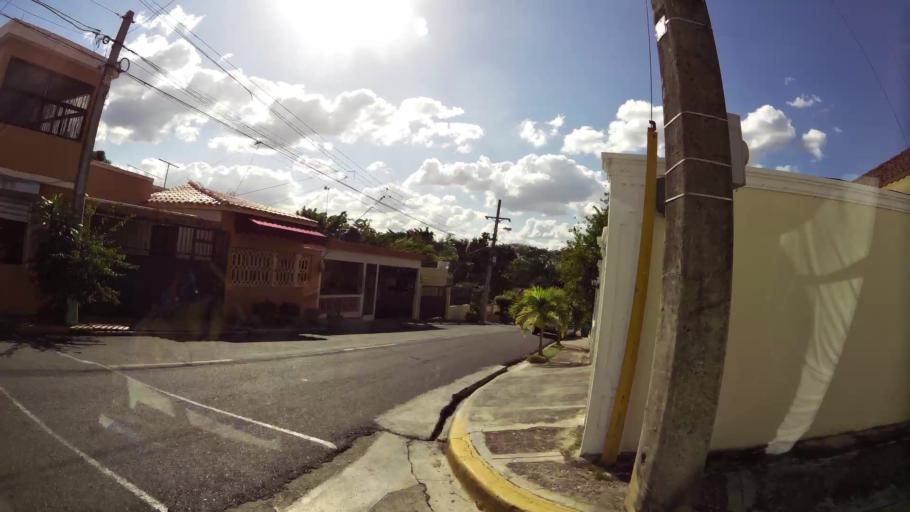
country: DO
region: Nacional
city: Santo Domingo
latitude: 18.5111
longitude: -69.9866
